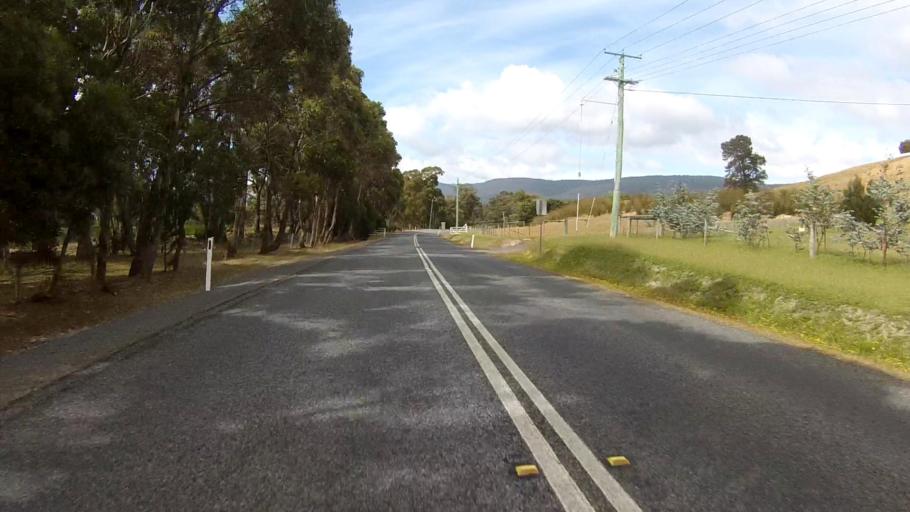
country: AU
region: Tasmania
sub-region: Kingborough
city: Kettering
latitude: -43.1501
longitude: 147.2400
